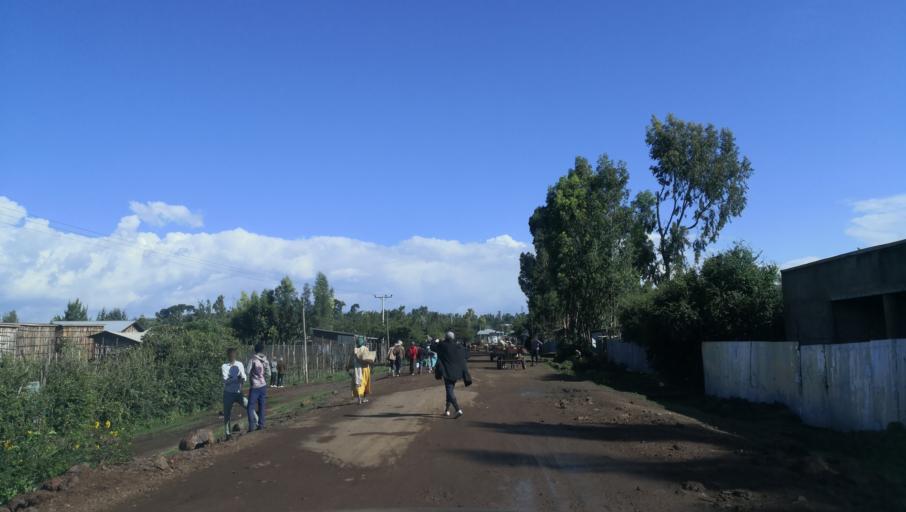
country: ET
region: Oromiya
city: Tulu Bolo
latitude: 8.6558
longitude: 38.2181
